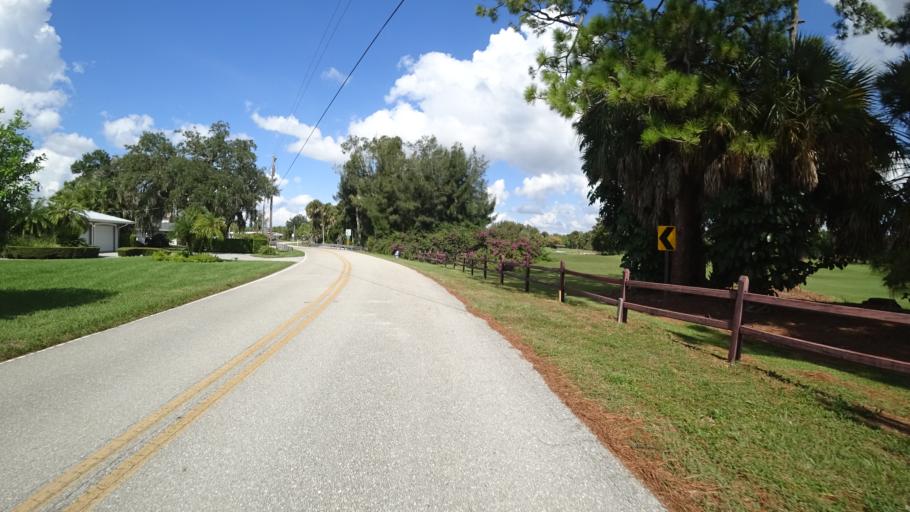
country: US
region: Florida
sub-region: Manatee County
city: Whitfield
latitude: 27.4182
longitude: -82.5647
